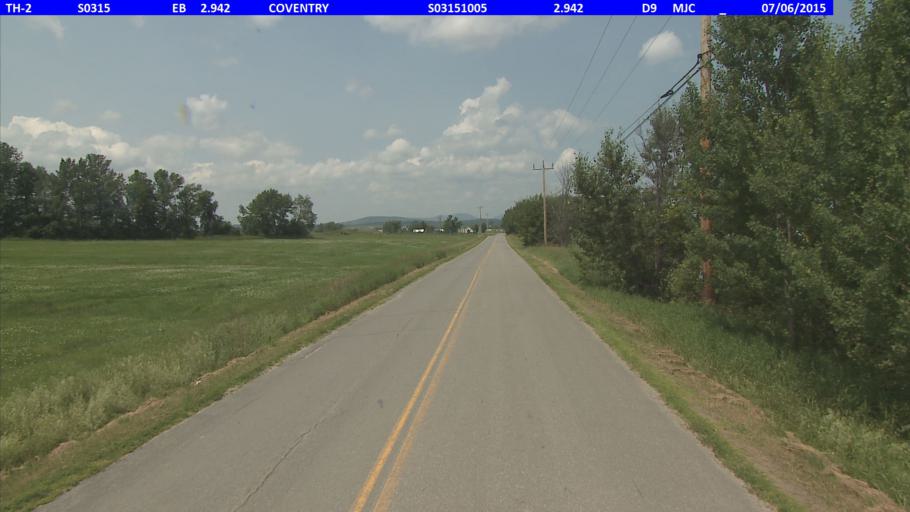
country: US
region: Vermont
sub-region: Orleans County
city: Newport
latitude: 44.8785
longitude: -72.2166
